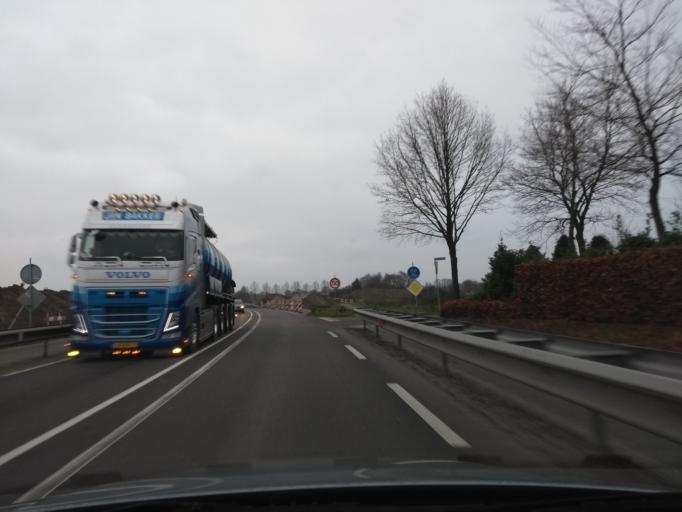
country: NL
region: Overijssel
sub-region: Gemeente Haaksbergen
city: Haaksbergen
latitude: 52.1836
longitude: 6.7375
